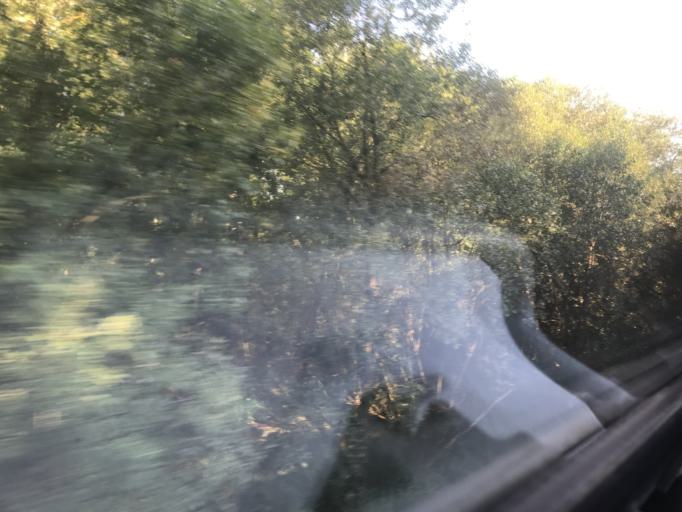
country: CZ
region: Jihocesky
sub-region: Okres Jindrichuv Hradec
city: Lomnice nad Luznici
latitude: 49.1246
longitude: 14.7387
